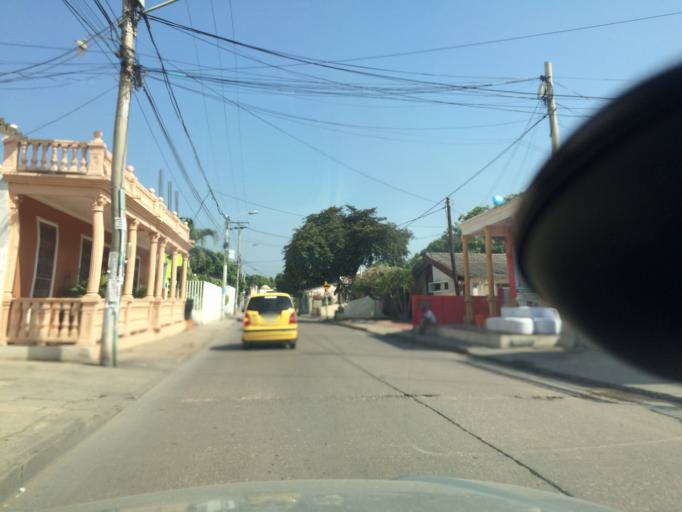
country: CO
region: Bolivar
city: Cartagena
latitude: 10.4158
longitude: -75.5355
